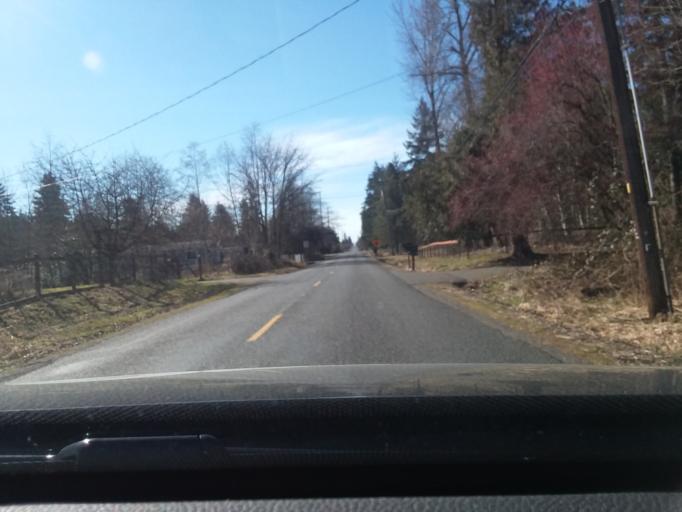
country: US
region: Washington
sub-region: Pierce County
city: Waller
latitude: 47.1824
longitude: -122.3786
